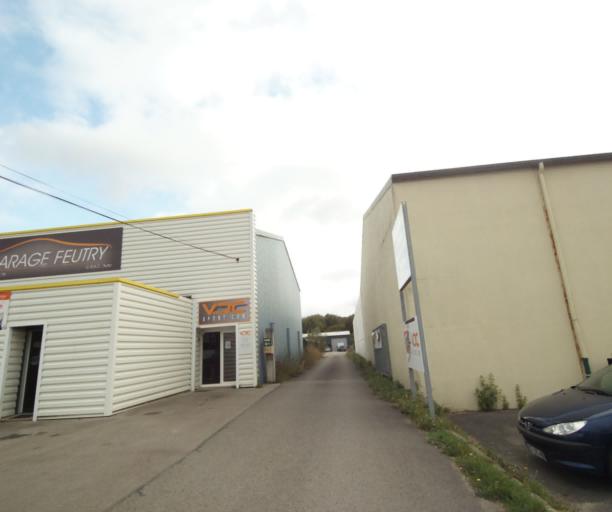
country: FR
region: Nord-Pas-de-Calais
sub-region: Departement du Pas-de-Calais
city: Etaples
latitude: 50.5193
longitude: 1.6627
